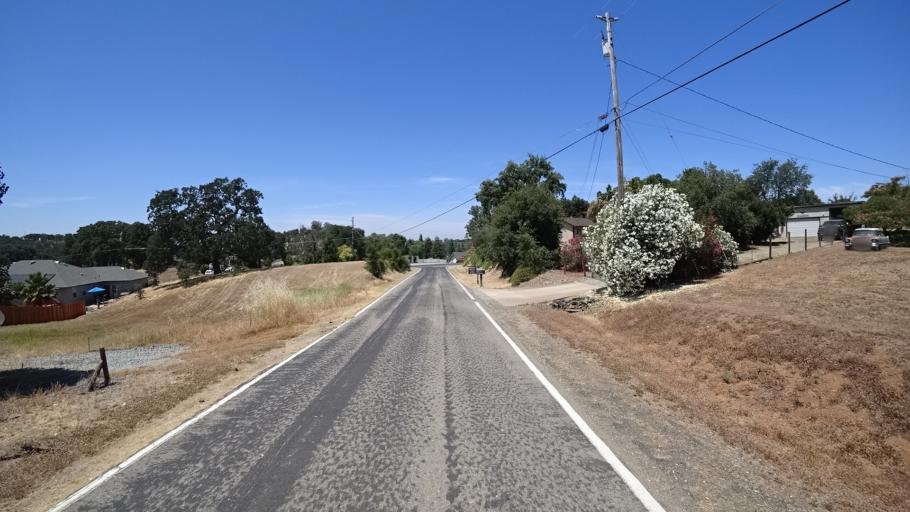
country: US
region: California
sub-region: Calaveras County
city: Rancho Calaveras
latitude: 38.1268
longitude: -120.8663
